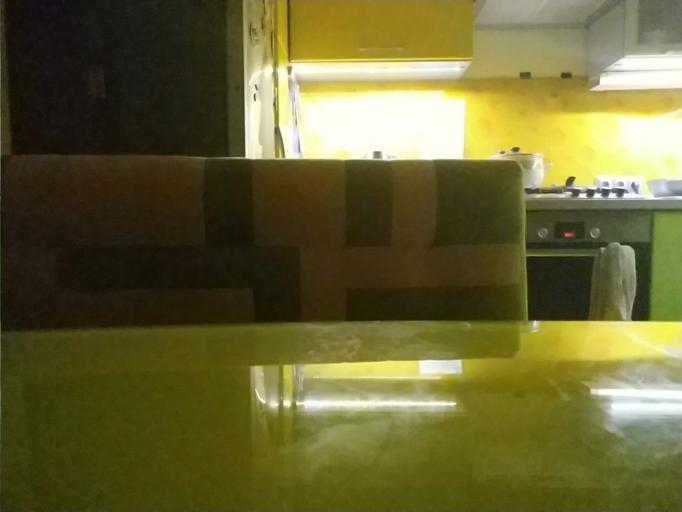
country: RU
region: Republic of Karelia
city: Pyaozerskiy
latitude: 65.6026
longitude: 30.5632
